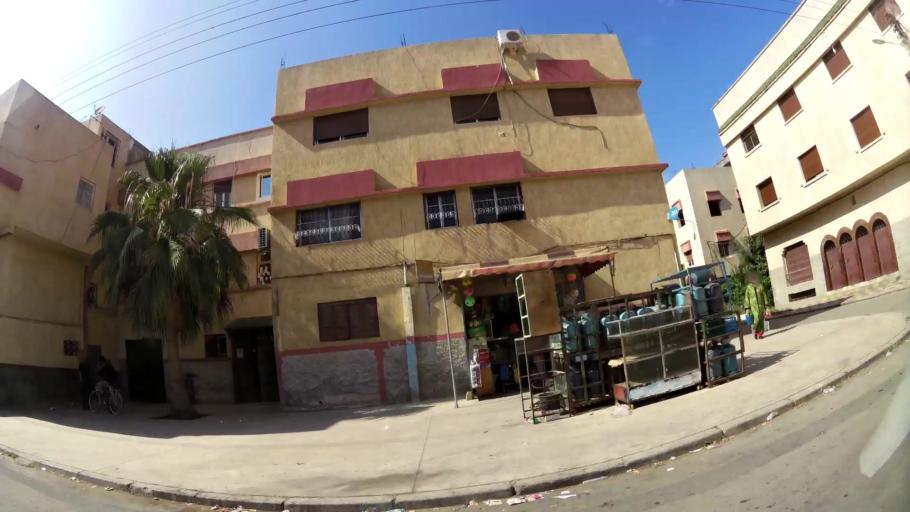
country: MA
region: Rabat-Sale-Zemmour-Zaer
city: Sale
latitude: 34.0438
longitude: -6.7817
